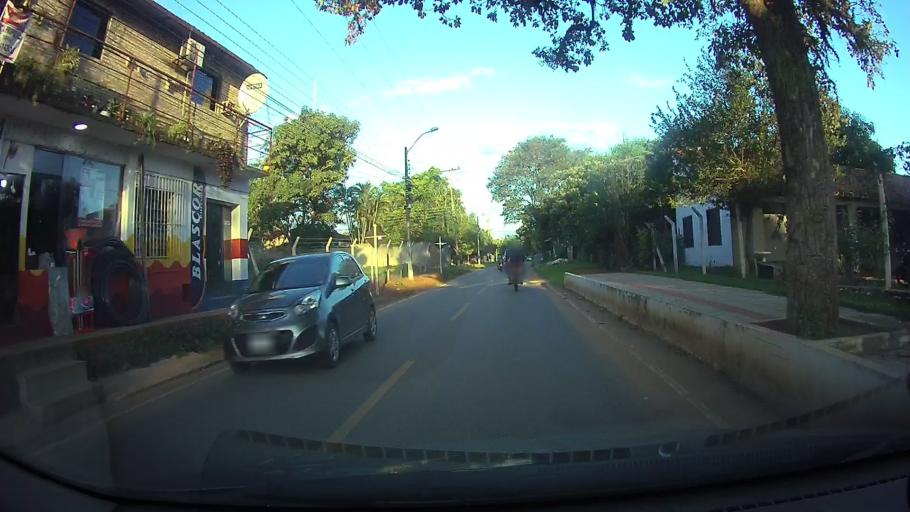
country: PY
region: Central
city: Fernando de la Mora
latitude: -25.2855
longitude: -57.5132
